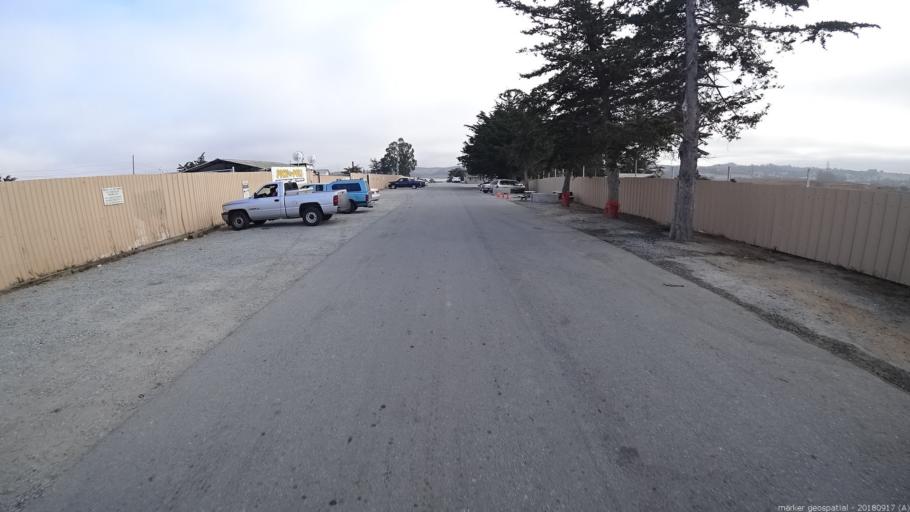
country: US
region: California
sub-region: Monterey County
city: Elkhorn
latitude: 36.8033
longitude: -121.7510
